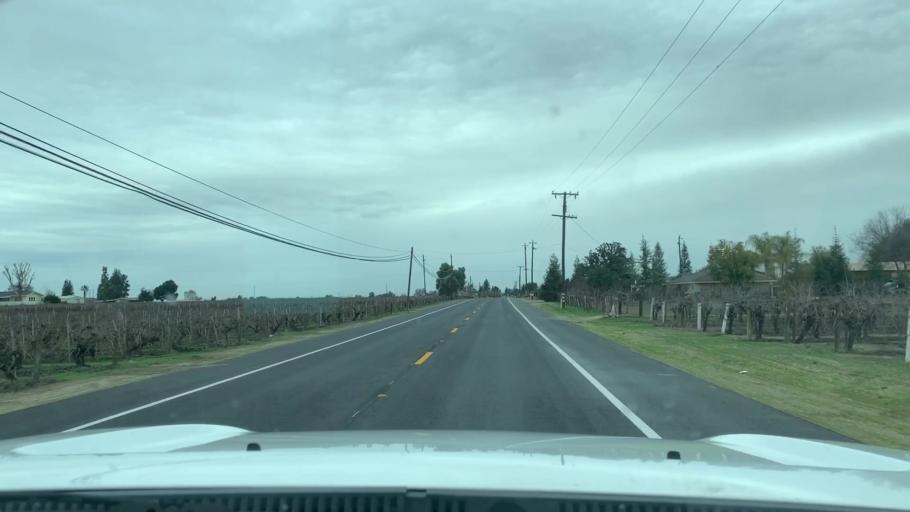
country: US
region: California
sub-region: Fresno County
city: Selma
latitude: 36.5505
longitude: -119.6827
